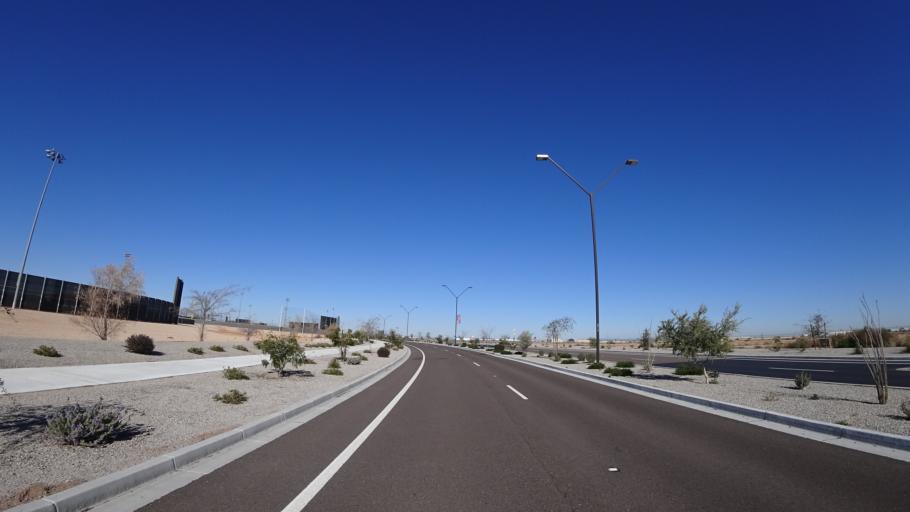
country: US
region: Arizona
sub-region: Maricopa County
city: Goodyear
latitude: 33.4149
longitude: -112.3881
